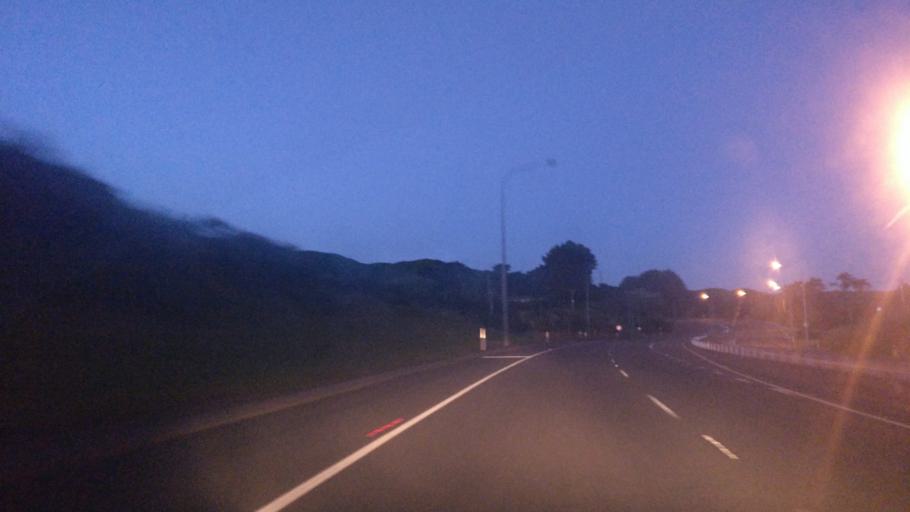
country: NZ
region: Wellington
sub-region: Porirua City
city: Porirua
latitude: -41.0570
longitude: 174.8761
